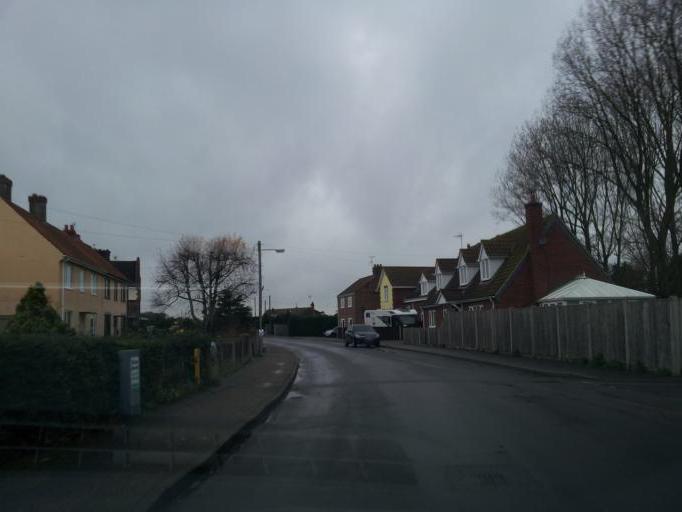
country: GB
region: England
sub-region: Norfolk
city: Hemsby
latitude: 52.6918
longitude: 1.6955
